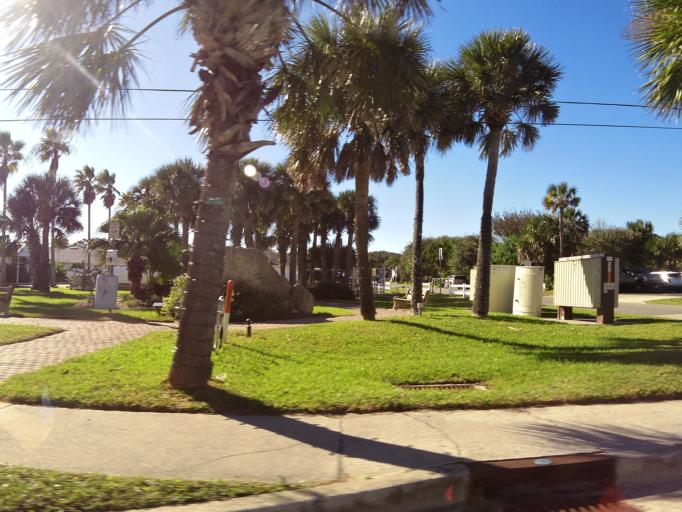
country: US
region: Florida
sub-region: Saint Johns County
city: Saint Augustine Beach
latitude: 29.8539
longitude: -81.2673
